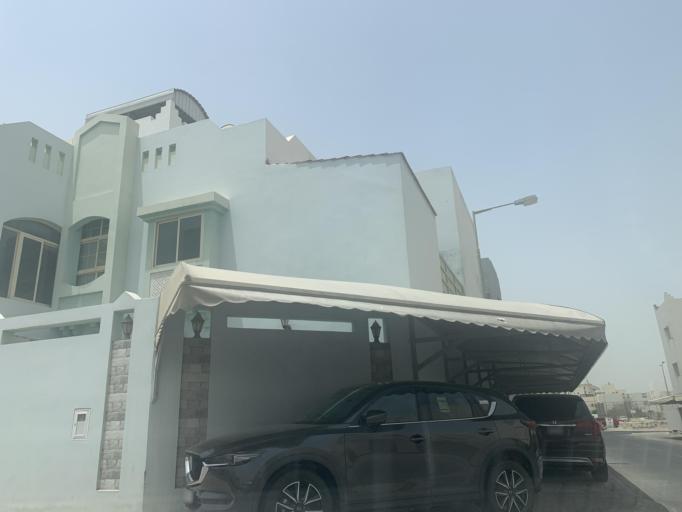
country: BH
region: Manama
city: Jidd Hafs
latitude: 26.2118
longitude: 50.5381
